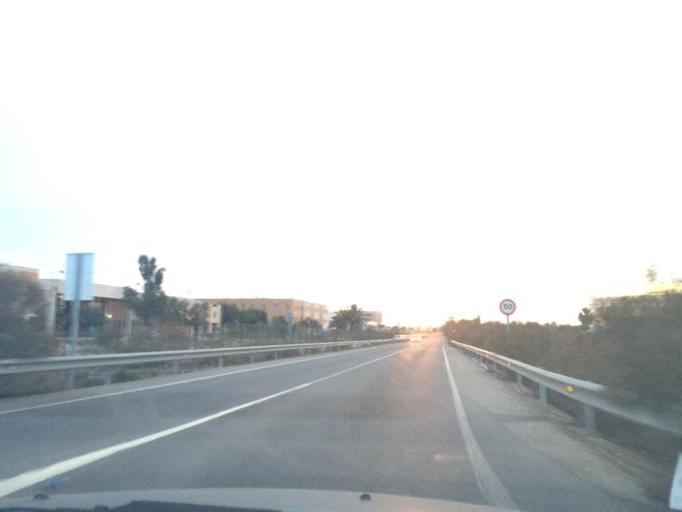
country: ES
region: Andalusia
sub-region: Provincia de Almeria
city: Almeria
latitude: 36.8322
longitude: -2.4040
